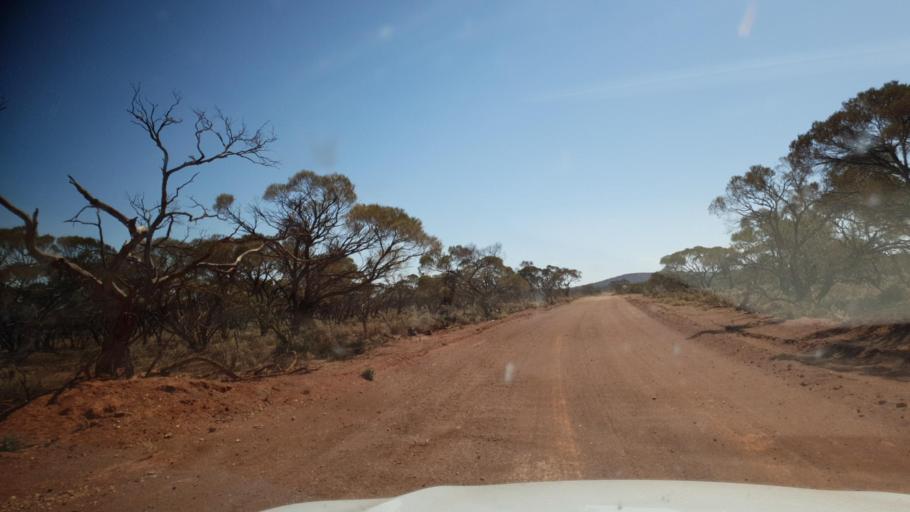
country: AU
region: South Australia
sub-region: Kimba
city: Caralue
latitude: -32.4869
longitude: 136.3802
